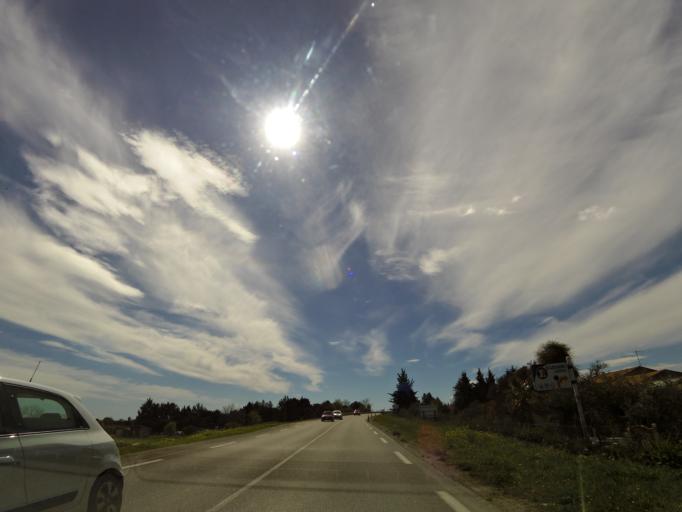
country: FR
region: Languedoc-Roussillon
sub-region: Departement de l'Herault
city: Lunel
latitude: 43.6805
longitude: 4.1508
